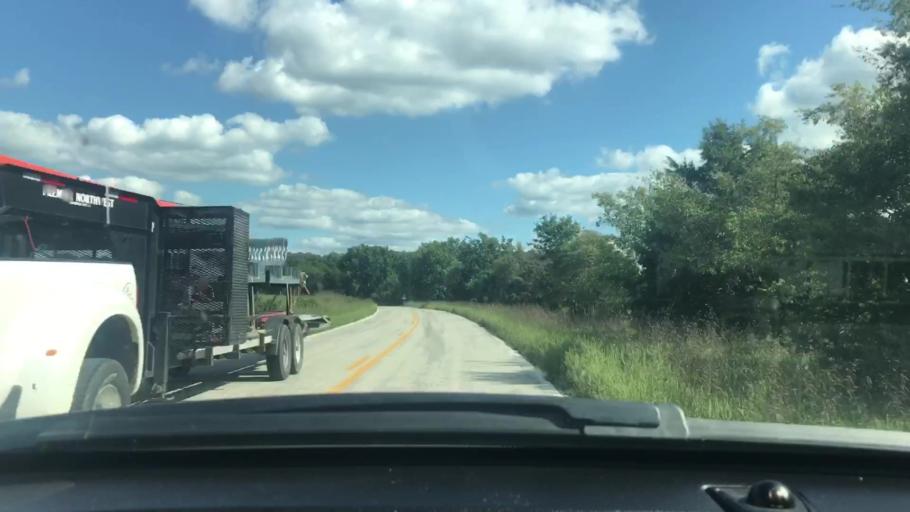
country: US
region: Missouri
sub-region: Wright County
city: Hartville
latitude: 37.3790
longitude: -92.4352
